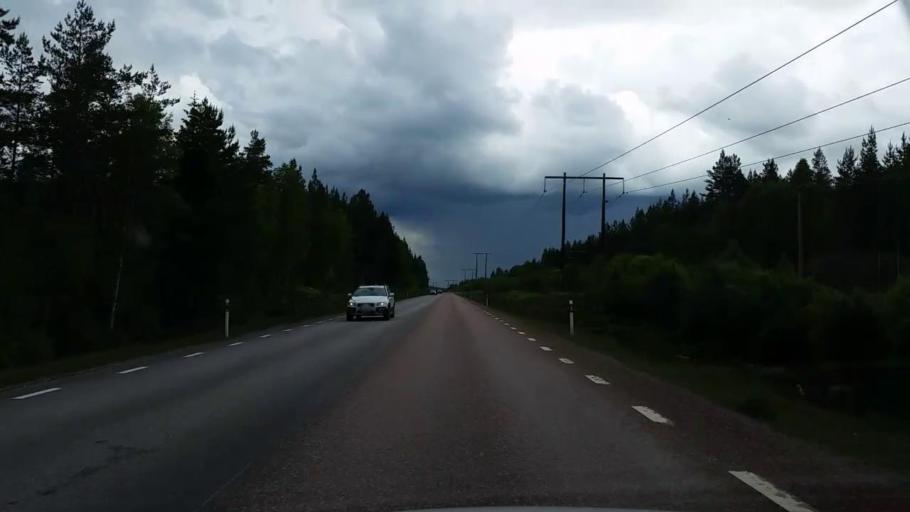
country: SE
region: Gaevleborg
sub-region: Hofors Kommun
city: Hofors
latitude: 60.5256
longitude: 16.4521
